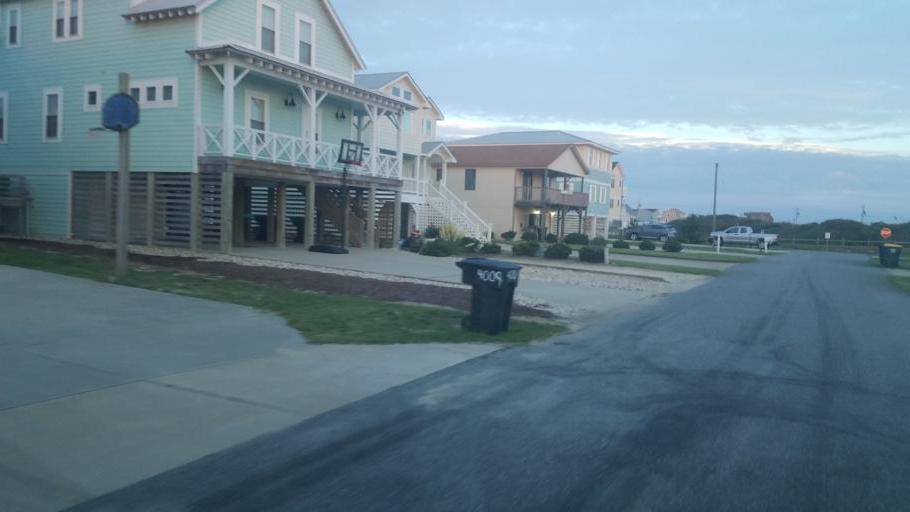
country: US
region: North Carolina
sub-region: Dare County
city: Kitty Hawk
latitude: 36.0714
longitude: -75.6948
